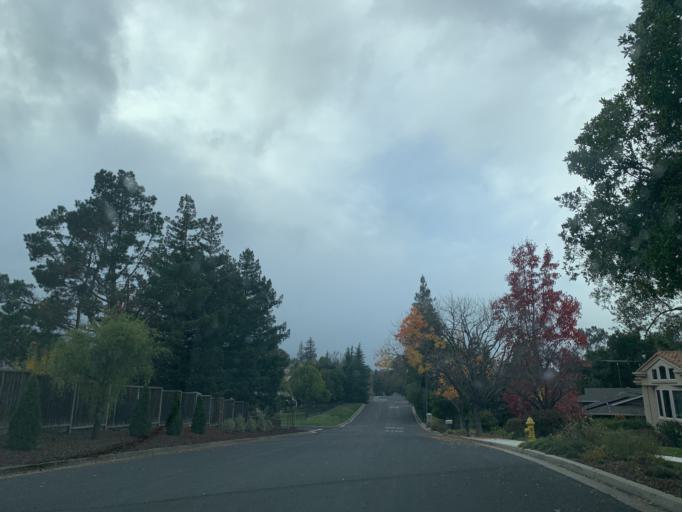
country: US
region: California
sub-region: Santa Clara County
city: Monte Sereno
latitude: 37.2501
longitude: -121.9856
